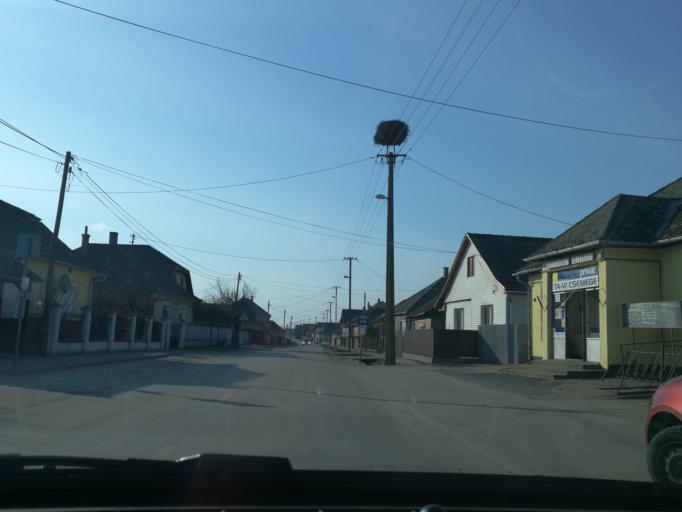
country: HU
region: Szabolcs-Szatmar-Bereg
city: Apagy
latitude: 48.0184
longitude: 21.9615
